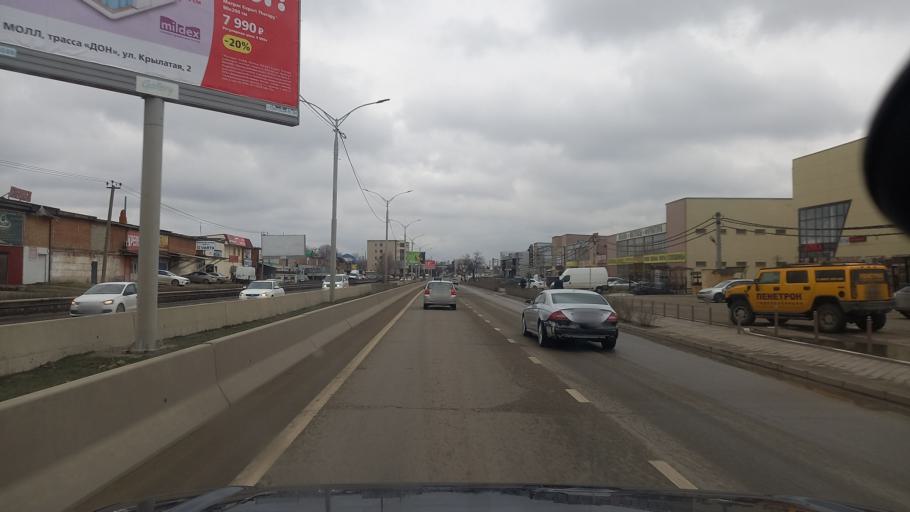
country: RU
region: Krasnodarskiy
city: Pashkovskiy
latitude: 45.0438
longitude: 39.1170
